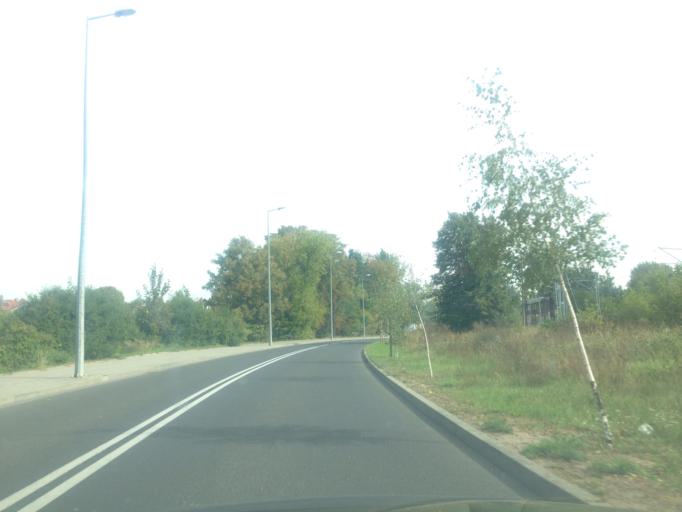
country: PL
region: Kujawsko-Pomorskie
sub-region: Powiat aleksandrowski
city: Ciechocinek
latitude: 52.8804
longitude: 18.7845
